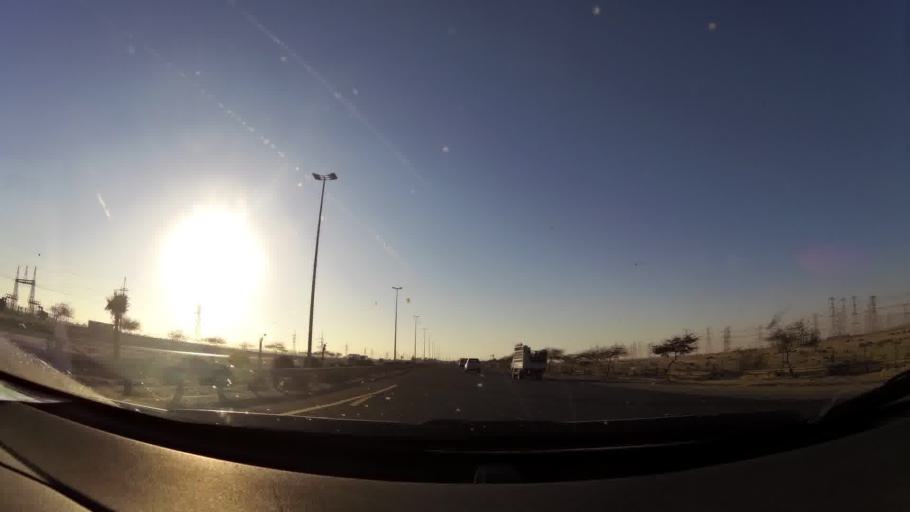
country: KW
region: Al Ahmadi
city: Al Fahahil
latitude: 28.8069
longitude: 48.2668
